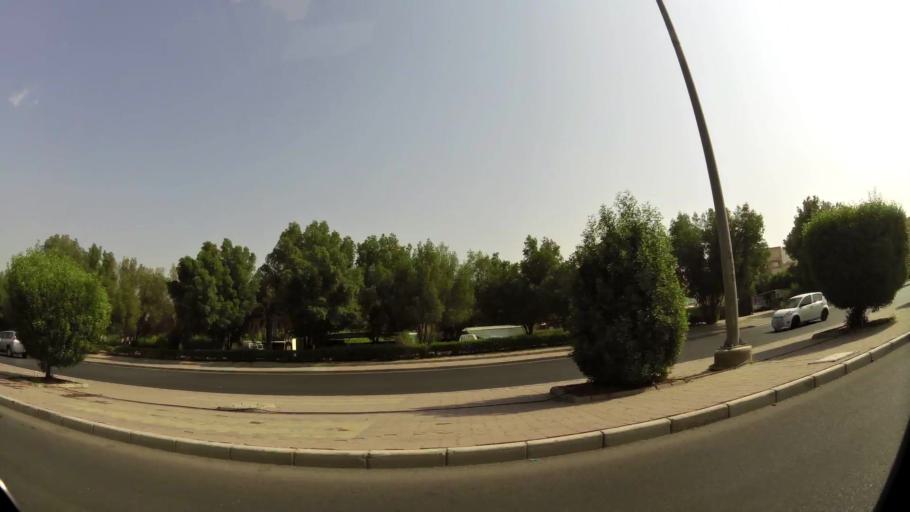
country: KW
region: Al Asimah
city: Ar Rabiyah
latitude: 29.2827
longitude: 47.8860
